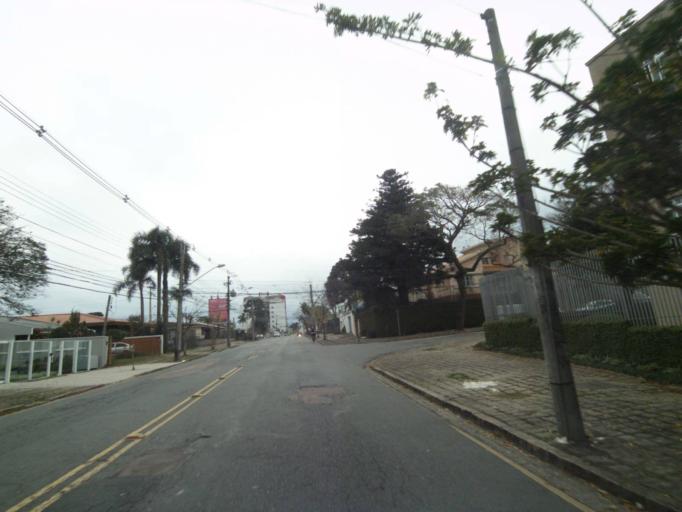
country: BR
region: Parana
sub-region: Curitiba
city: Curitiba
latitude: -25.4001
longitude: -49.2625
